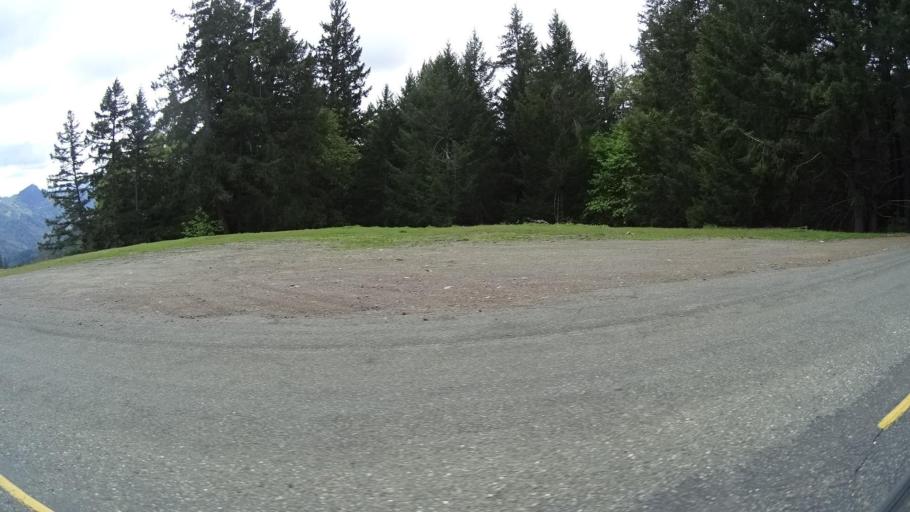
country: US
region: California
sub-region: Humboldt County
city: Redway
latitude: 40.1225
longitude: -123.6596
